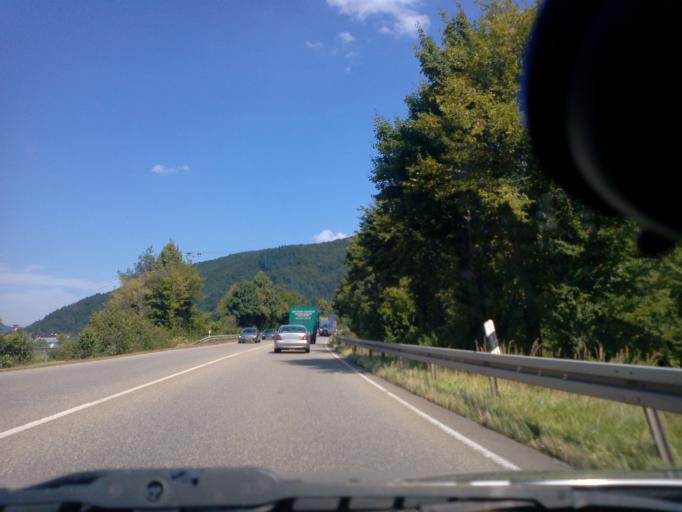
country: DE
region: Baden-Wuerttemberg
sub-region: Freiburg Region
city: Steinach
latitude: 48.2976
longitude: 8.0625
